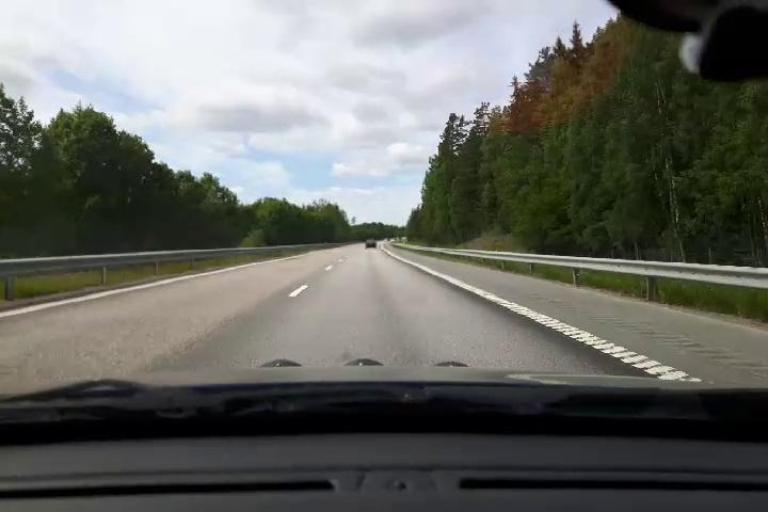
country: SE
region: Uppsala
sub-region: Alvkarleby Kommun
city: AElvkarleby
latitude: 60.4740
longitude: 17.3839
